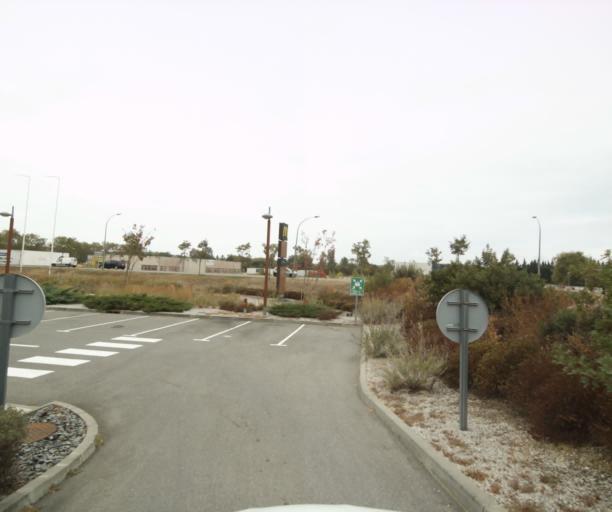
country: FR
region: Midi-Pyrenees
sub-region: Departement de la Haute-Garonne
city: Villefranche-de-Lauragais
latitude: 43.3991
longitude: 1.7035
